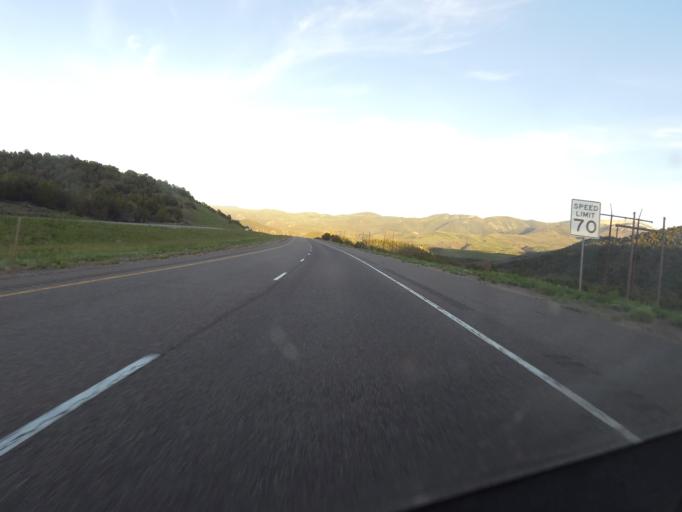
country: US
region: Utah
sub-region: Beaver County
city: Beaver
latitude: 38.5795
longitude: -112.4808
